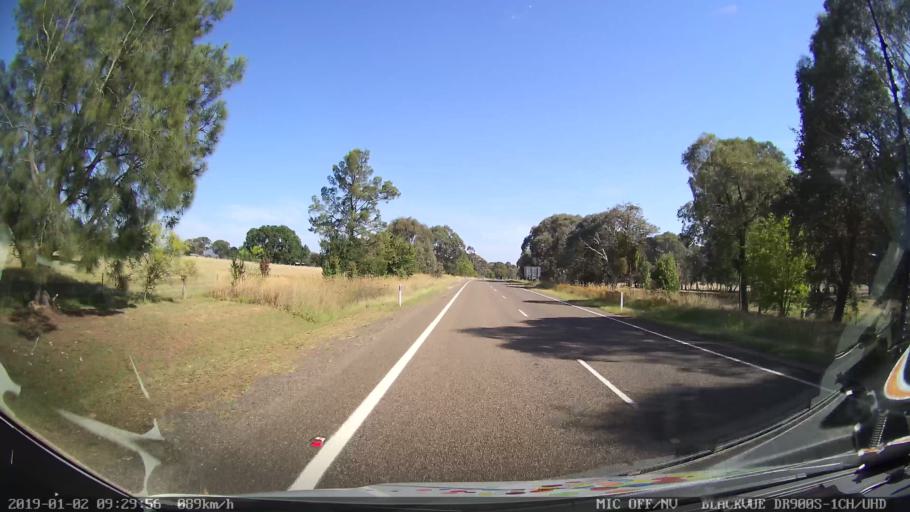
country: AU
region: New South Wales
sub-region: Tumut Shire
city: Tumut
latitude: -35.3330
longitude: 148.2385
